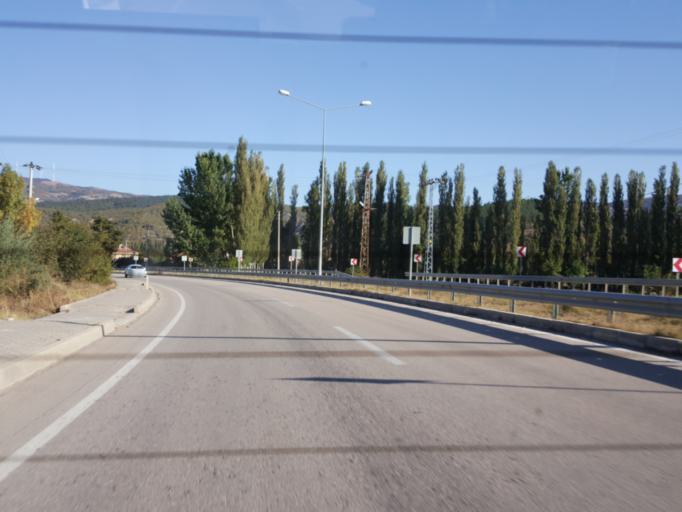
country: TR
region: Amasya
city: Ezinepazari
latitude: 40.5673
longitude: 36.1402
